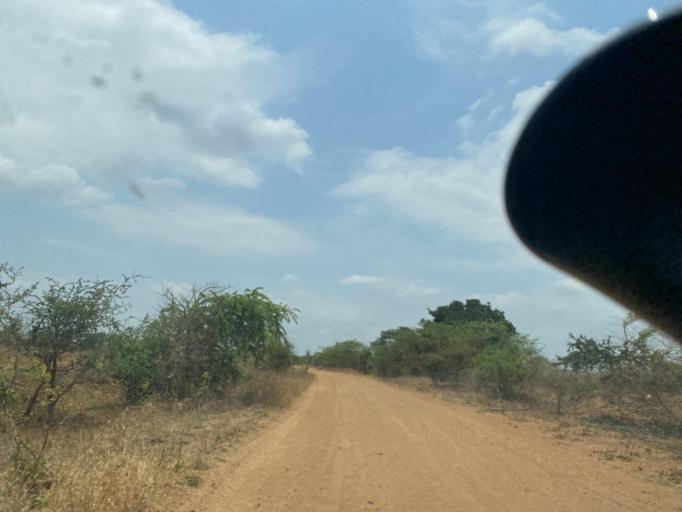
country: ZM
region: Lusaka
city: Chongwe
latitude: -15.5254
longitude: 28.8234
